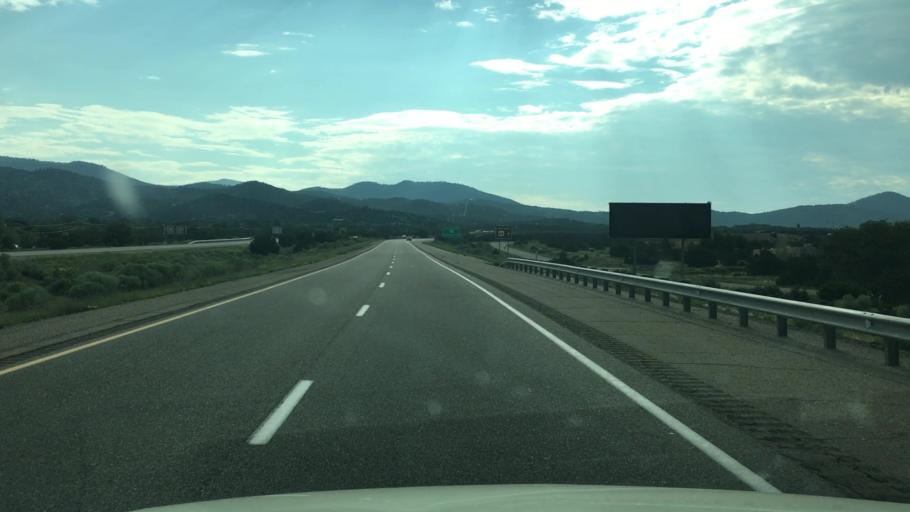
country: US
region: New Mexico
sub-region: Santa Fe County
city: Santa Fe
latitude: 35.6371
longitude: -105.9419
